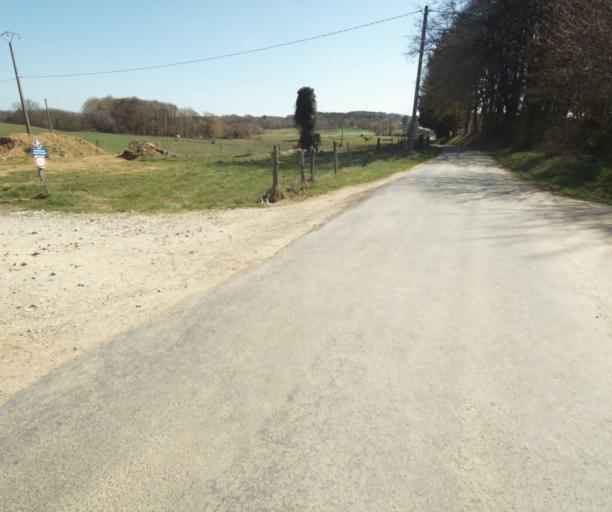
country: FR
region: Limousin
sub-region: Departement de la Correze
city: Saint-Mexant
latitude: 45.2902
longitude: 1.6855
